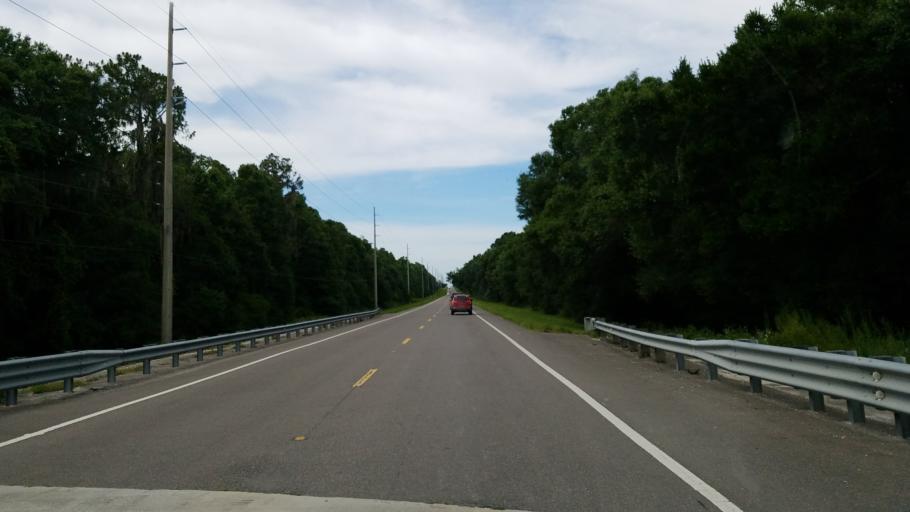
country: US
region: Florida
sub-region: Hillsborough County
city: Balm
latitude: 27.6885
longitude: -82.1461
